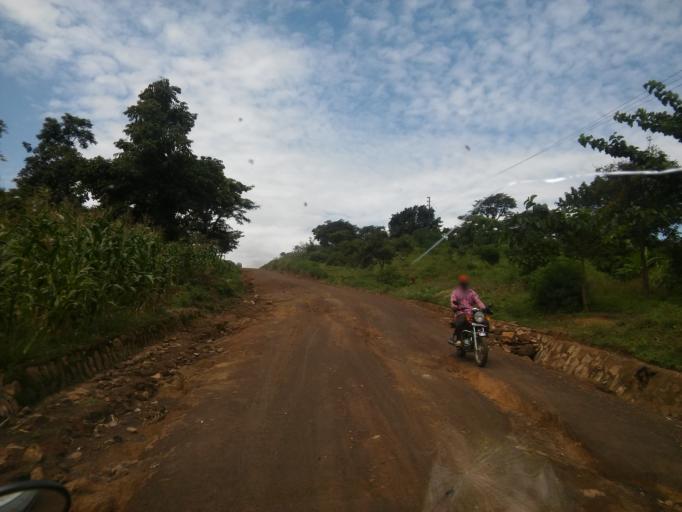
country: UG
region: Eastern Region
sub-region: Tororo District
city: Tororo
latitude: 0.8170
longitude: 34.2990
